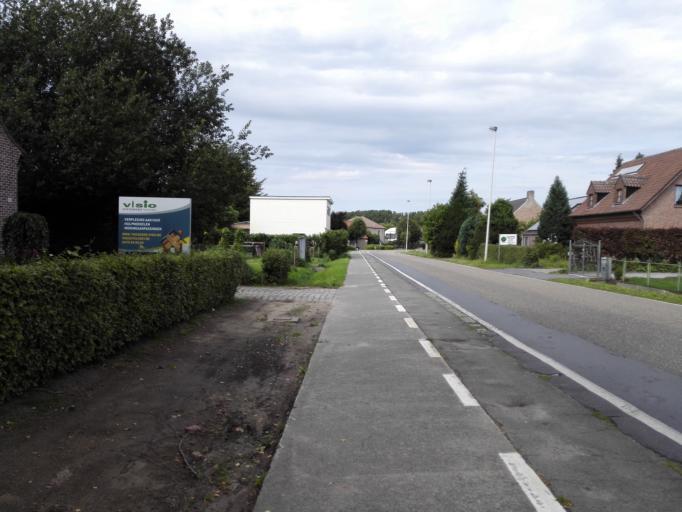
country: BE
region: Flanders
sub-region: Provincie Antwerpen
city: Schelle
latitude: 51.1234
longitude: 4.3602
